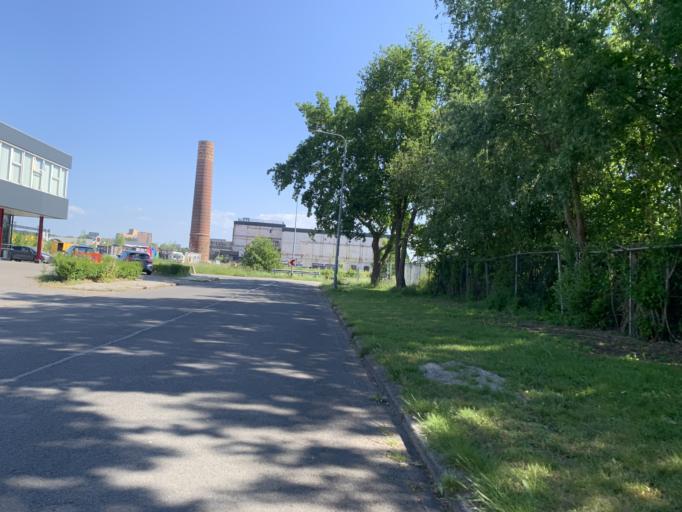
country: NL
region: Groningen
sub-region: Gemeente Groningen
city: Groningen
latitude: 53.2123
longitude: 6.5363
